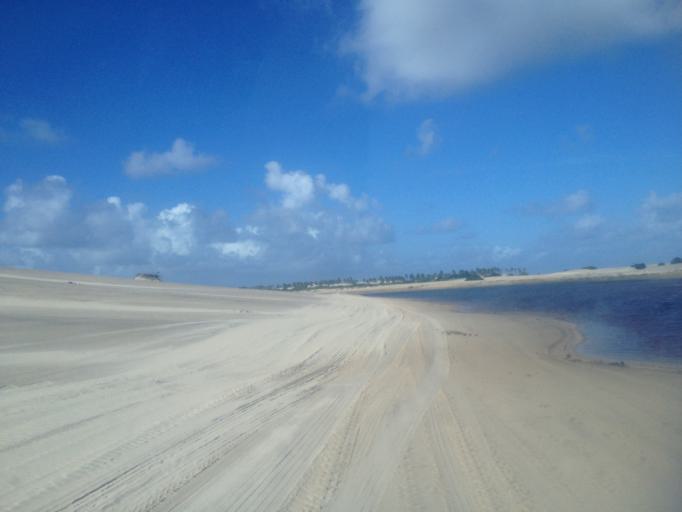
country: BR
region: Sergipe
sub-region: Indiaroba
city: Indiaroba
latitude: -11.4756
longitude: -37.3746
